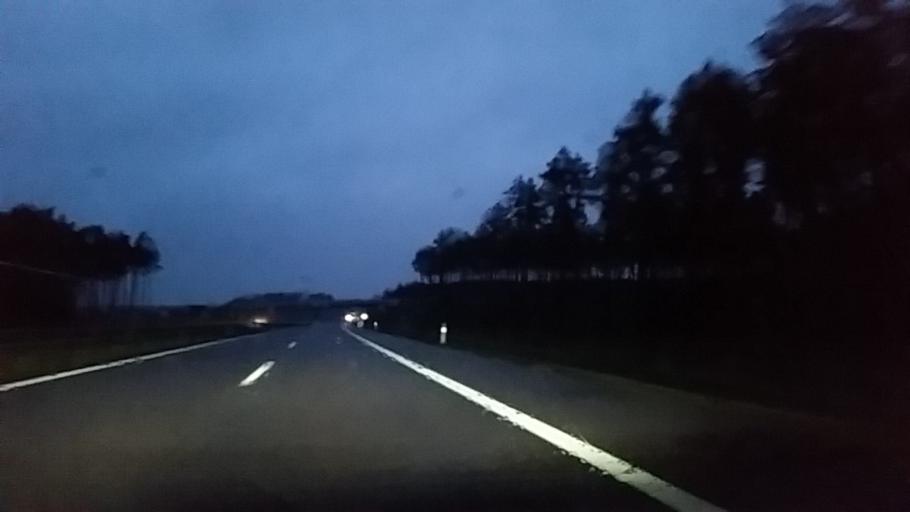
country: DE
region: Mecklenburg-Vorpommern
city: Ludwigslust
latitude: 53.3564
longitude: 11.5158
